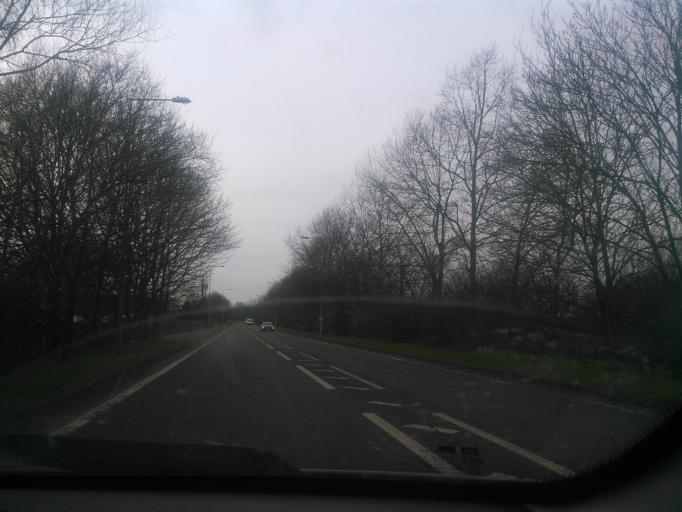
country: GB
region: England
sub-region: Telford and Wrekin
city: Oakengates
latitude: 52.7231
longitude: -2.4389
